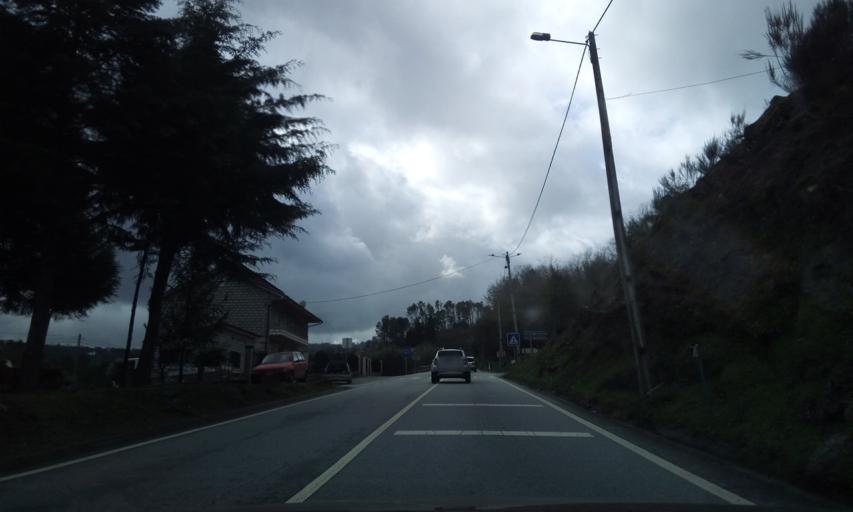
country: PT
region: Viseu
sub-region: Mangualde
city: Mangualde
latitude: 40.6393
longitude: -7.7396
